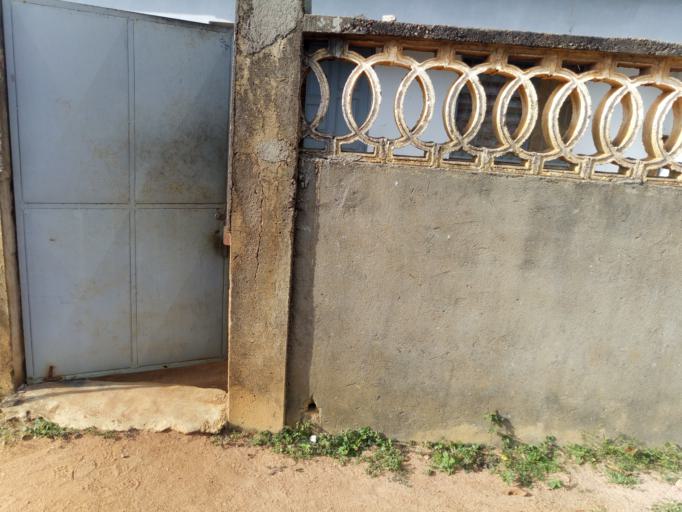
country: CI
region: Vallee du Bandama
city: Bouake
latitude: 7.6891
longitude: -5.0842
